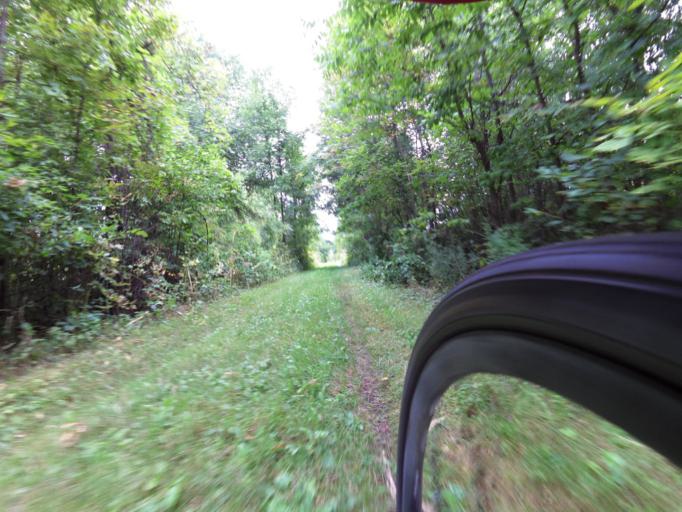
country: CA
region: Ontario
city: Perth
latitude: 44.6376
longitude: -76.2366
